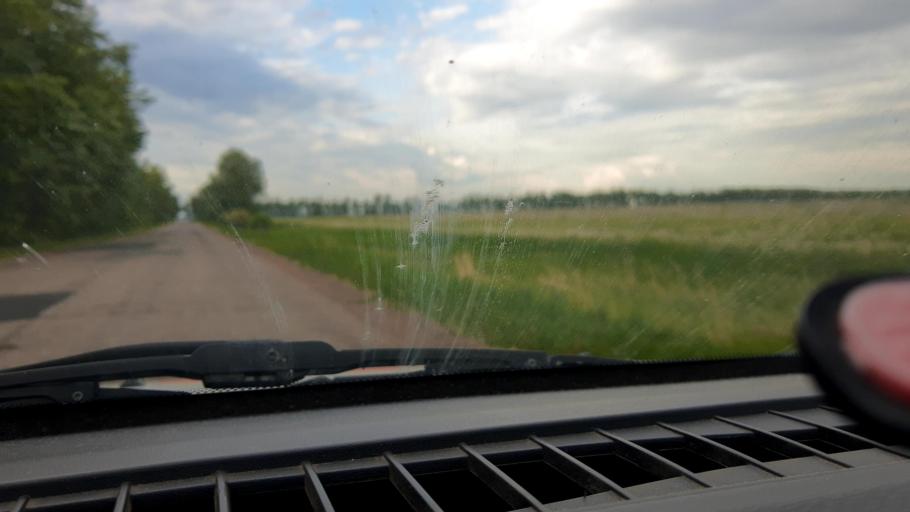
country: RU
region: Bashkortostan
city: Asanovo
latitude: 54.8259
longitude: 55.5971
